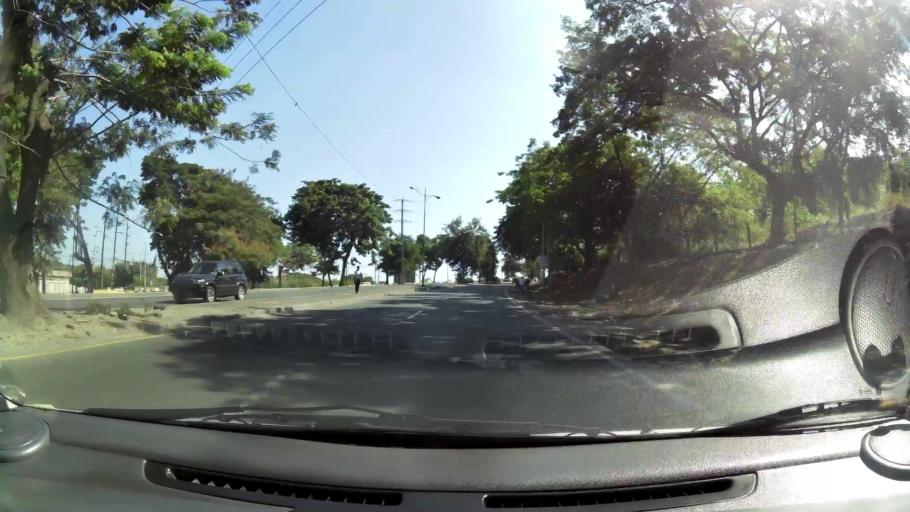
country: EC
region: Guayas
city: Guayaquil
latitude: -2.1873
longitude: -79.9488
